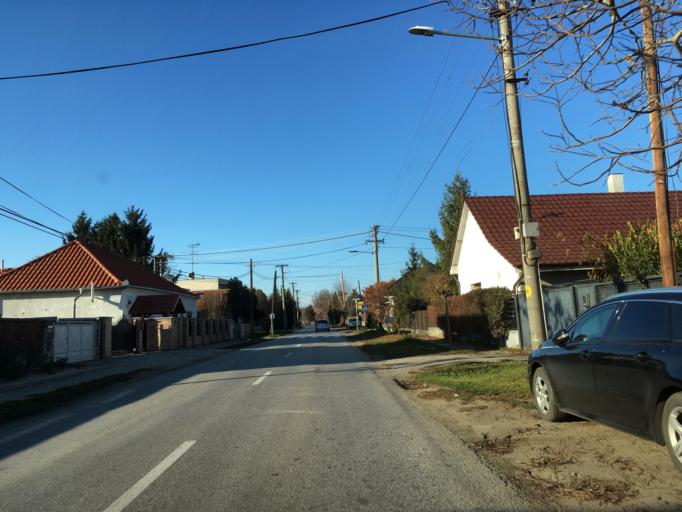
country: SK
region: Nitriansky
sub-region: Okres Nove Zamky
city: Nove Zamky
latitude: 47.9216
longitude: 18.1314
